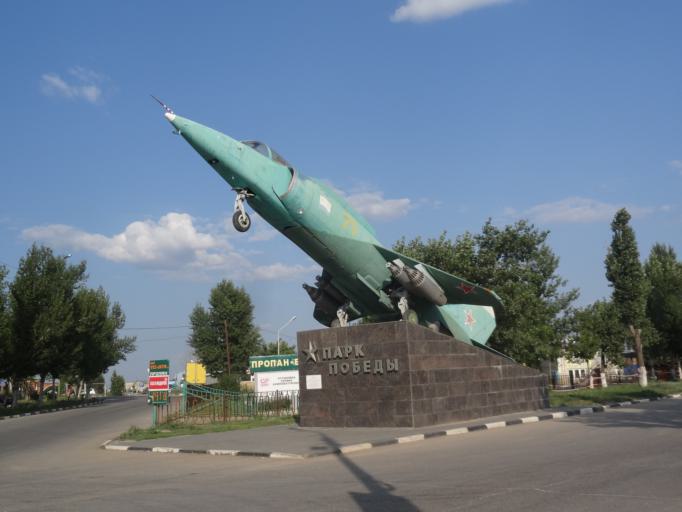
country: RU
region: Saratov
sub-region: Saratovskiy Rayon
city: Saratov
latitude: 51.5500
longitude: 46.0526
